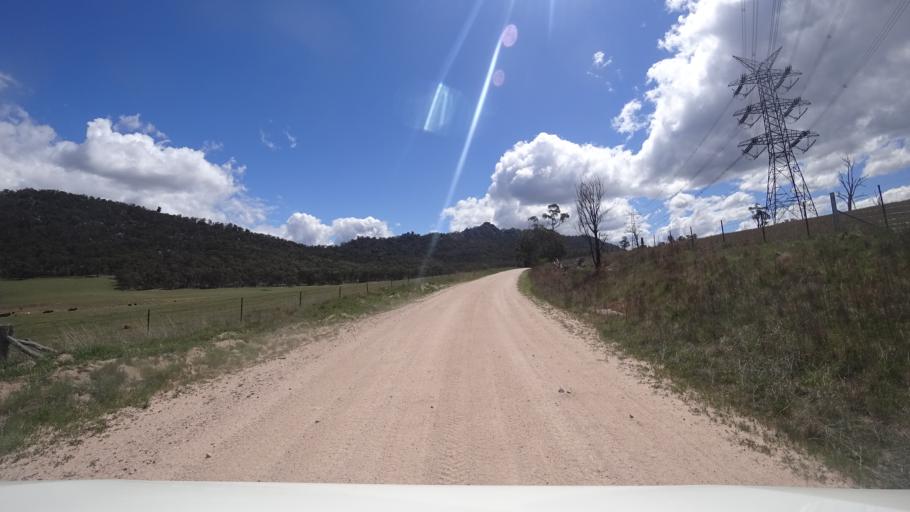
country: AU
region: New South Wales
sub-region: Oberon
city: Oberon
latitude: -33.5572
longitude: 149.9335
